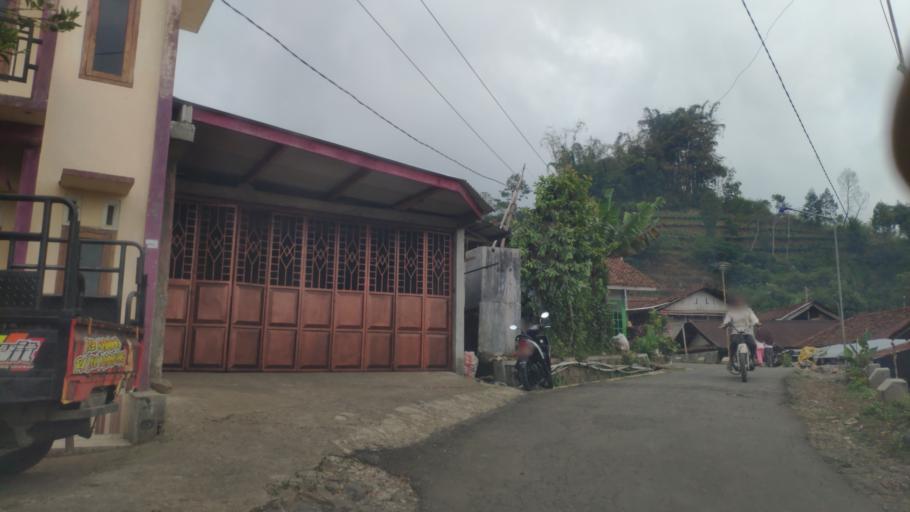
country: ID
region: Central Java
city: Wonosobo
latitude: -7.2445
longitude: 109.7961
